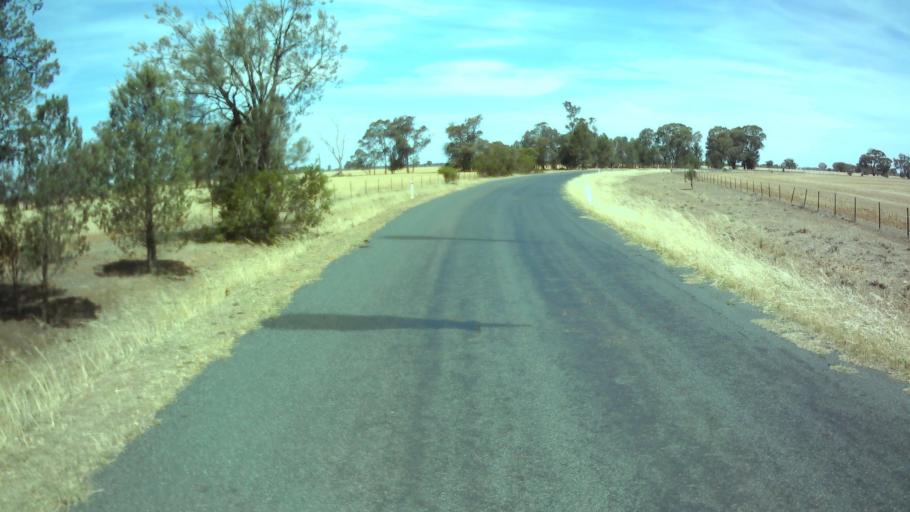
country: AU
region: New South Wales
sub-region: Weddin
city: Grenfell
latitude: -33.9583
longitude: 147.7804
